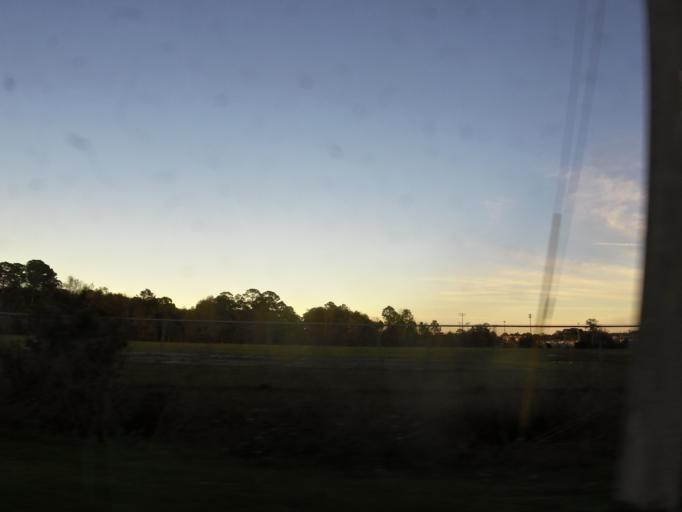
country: US
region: Florida
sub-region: Duval County
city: Jacksonville
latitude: 30.3475
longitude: -81.7292
